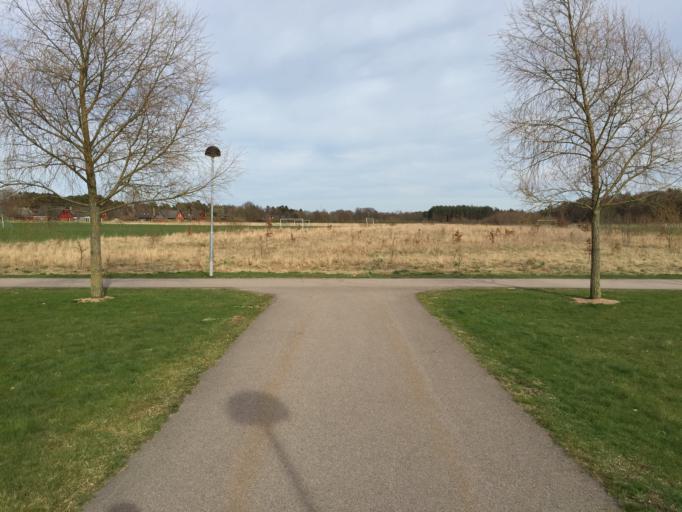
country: SE
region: Skane
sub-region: Lunds Kommun
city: Veberod
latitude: 55.6279
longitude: 13.5030
